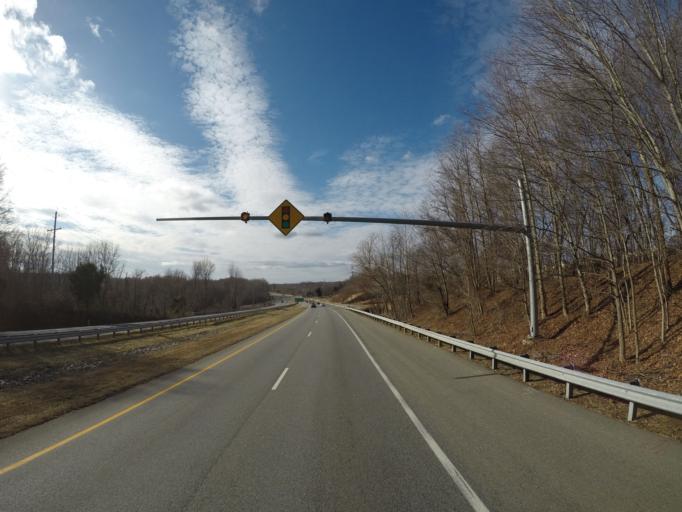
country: US
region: Maryland
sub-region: Charles County
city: Waldorf
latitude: 38.6522
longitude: -76.9690
